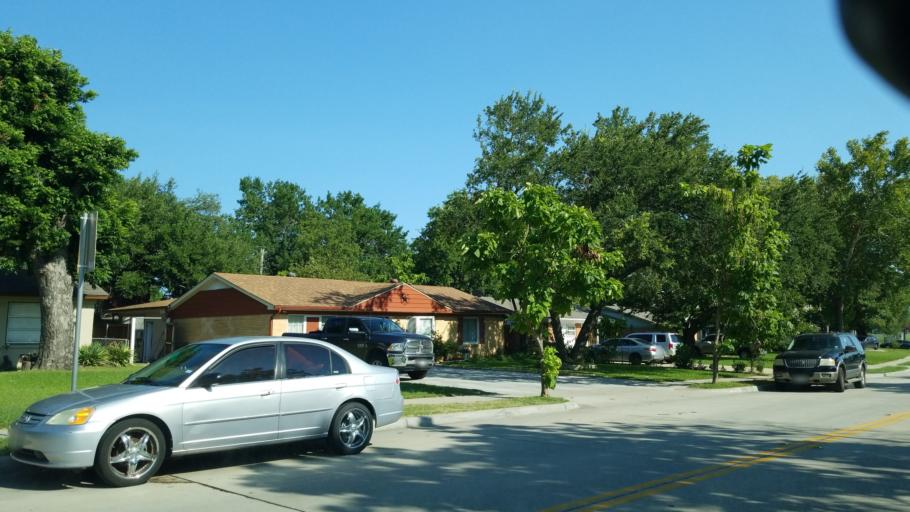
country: US
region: Texas
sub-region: Dallas County
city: Farmers Branch
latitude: 32.9307
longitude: -96.8904
